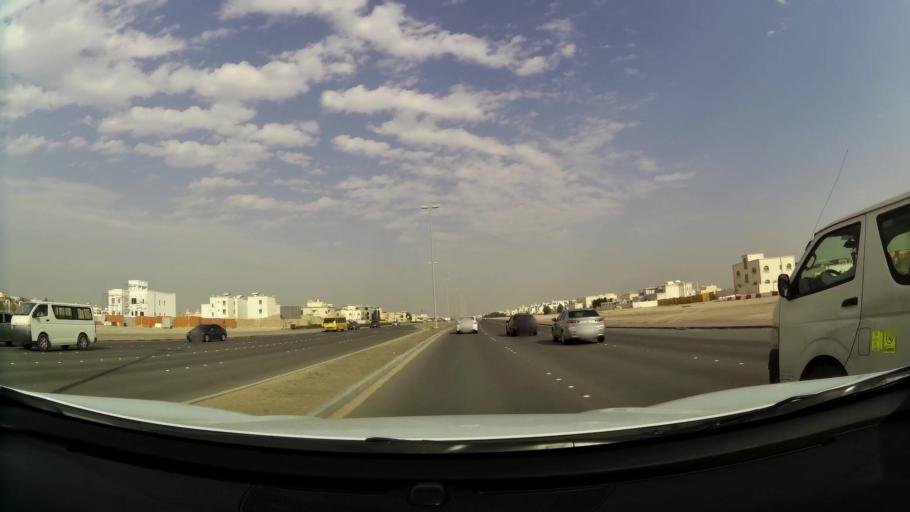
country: AE
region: Abu Dhabi
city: Abu Dhabi
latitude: 24.3248
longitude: 54.5403
